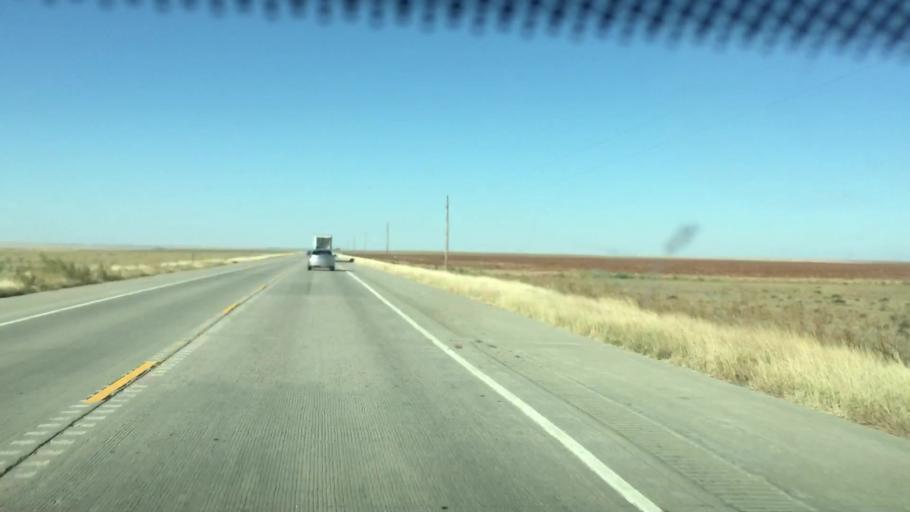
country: US
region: Colorado
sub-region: Kiowa County
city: Eads
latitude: 38.2881
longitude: -102.7199
